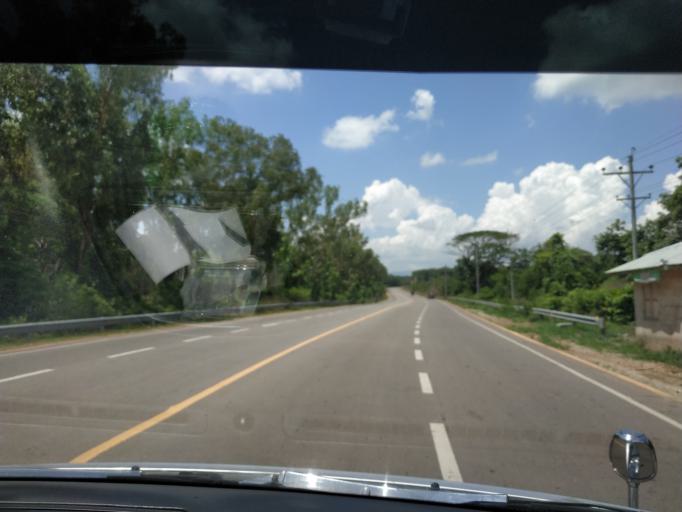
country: MM
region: Mon
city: Kyaikto
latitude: 17.3179
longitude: 97.0197
